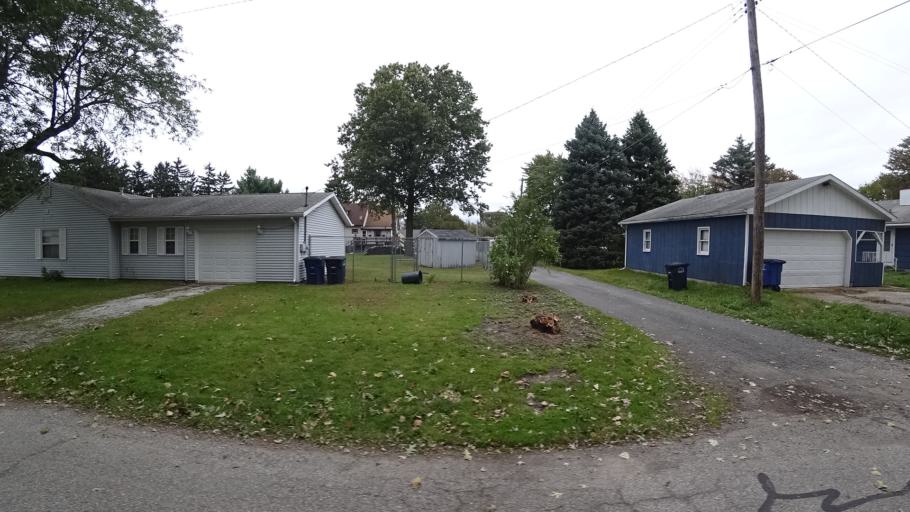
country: US
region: Indiana
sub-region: LaPorte County
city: Michigan City
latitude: 41.6983
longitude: -86.9001
